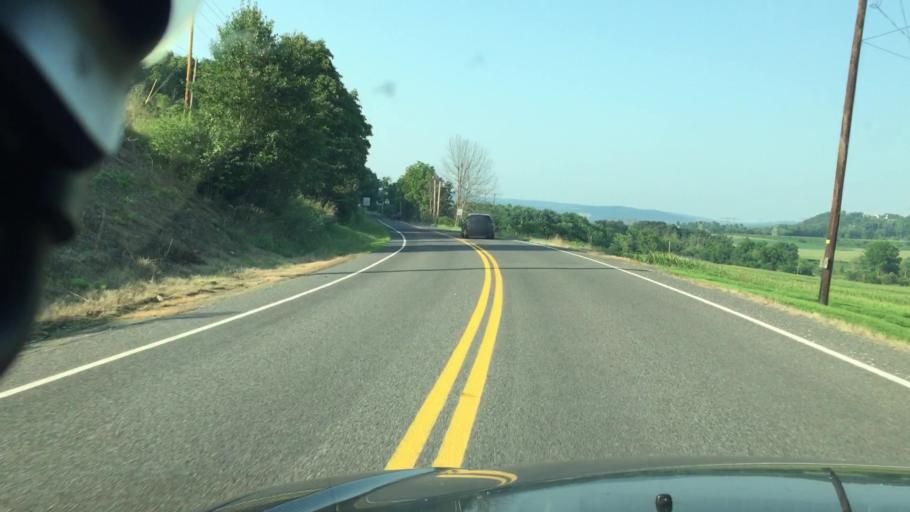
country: US
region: Pennsylvania
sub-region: Columbia County
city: Mifflinville
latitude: 41.0069
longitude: -76.3202
